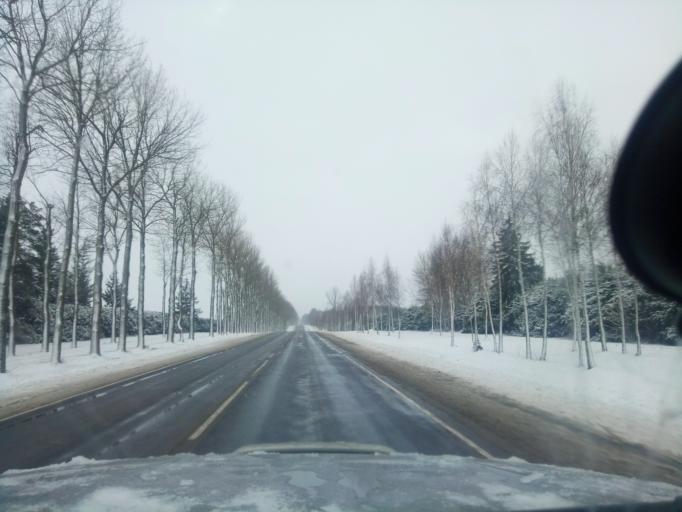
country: BY
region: Minsk
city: Haradzyeya
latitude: 53.3459
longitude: 26.5187
